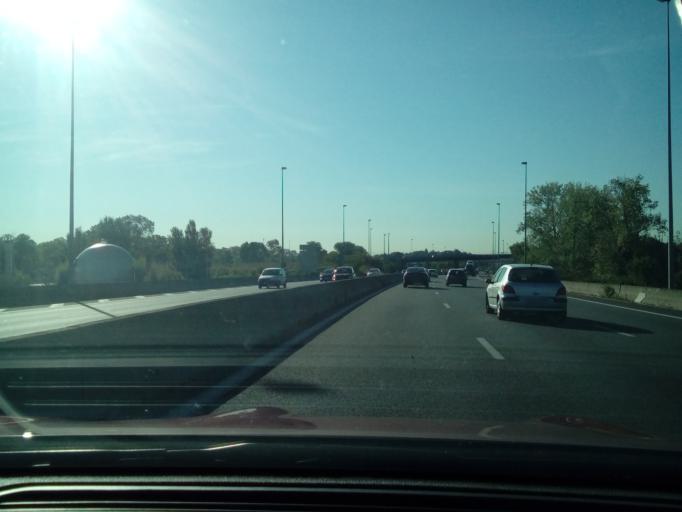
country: FR
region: Rhone-Alpes
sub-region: Departement du Rhone
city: Villeurbanne
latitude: 45.7924
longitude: 4.8817
